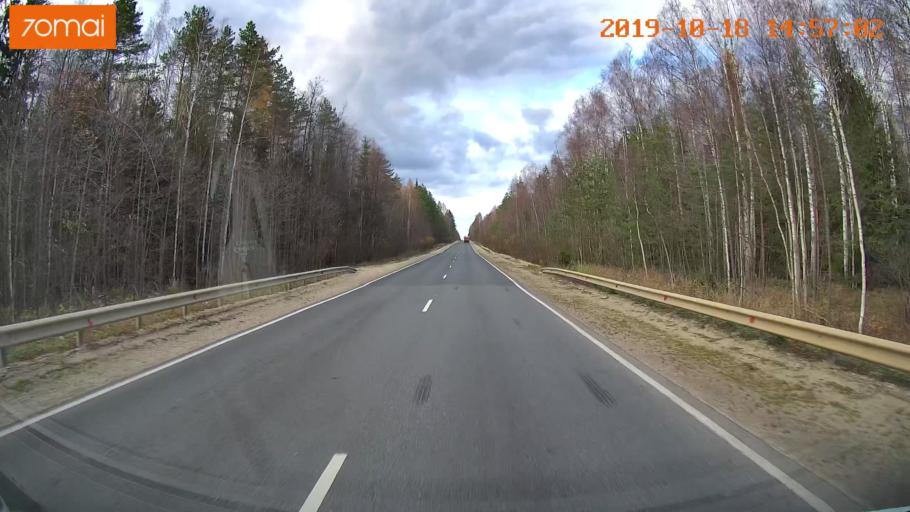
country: RU
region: Vladimir
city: Kurlovo
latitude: 55.4737
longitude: 40.5838
